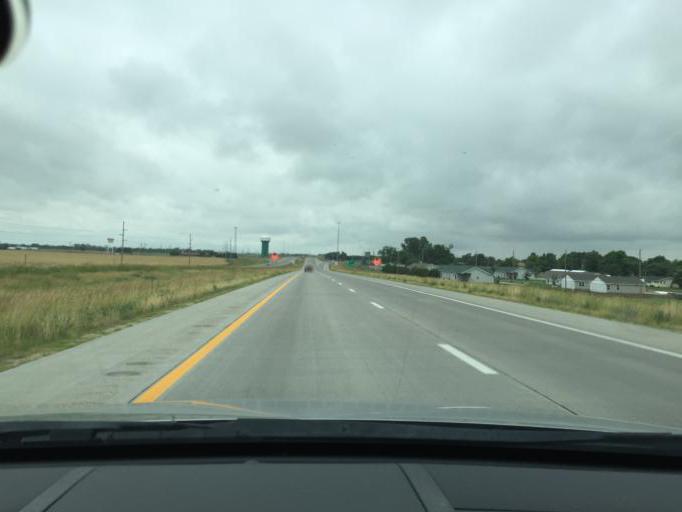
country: US
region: Kansas
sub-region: Reno County
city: South Hutchinson
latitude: 38.0133
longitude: -97.9319
